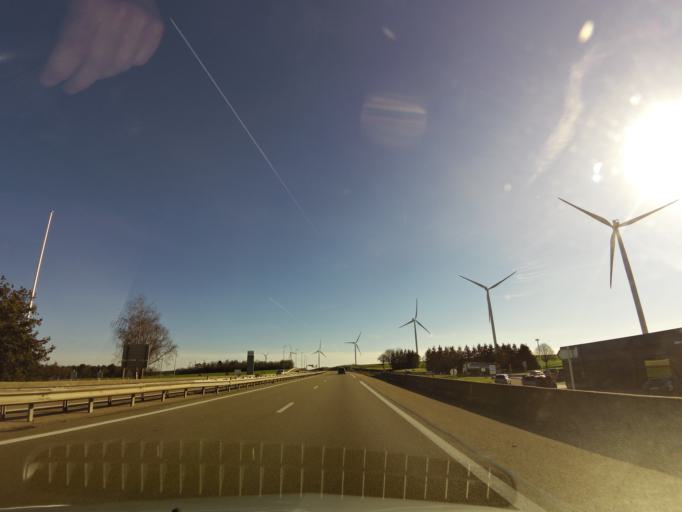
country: FR
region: Bourgogne
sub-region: Departement de l'Yonne
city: Venoy
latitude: 47.7872
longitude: 3.6719
